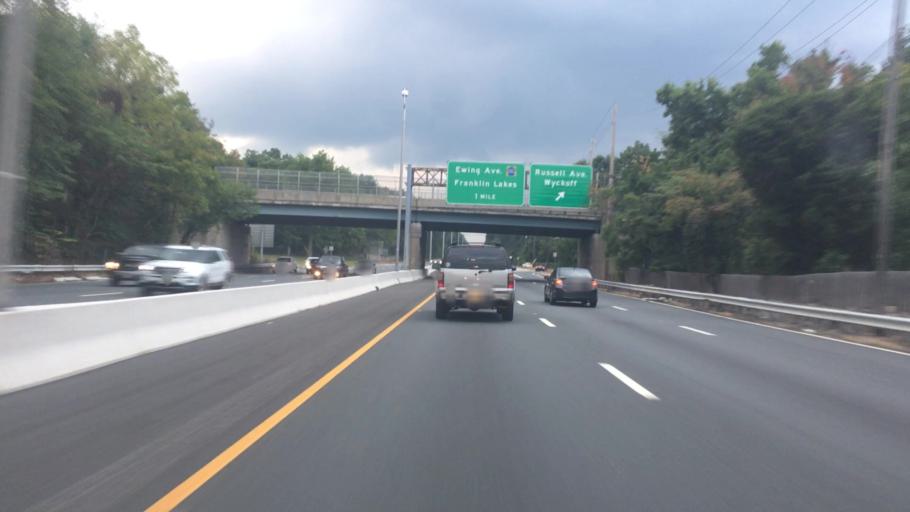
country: US
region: New Jersey
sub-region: Bergen County
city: Wyckoff
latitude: 40.9968
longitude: -74.1796
